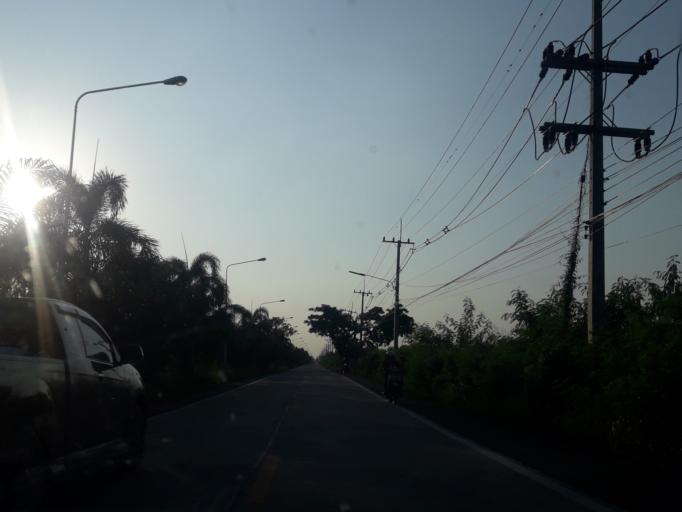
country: TH
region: Pathum Thani
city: Nong Suea
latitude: 14.1363
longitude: 100.8597
